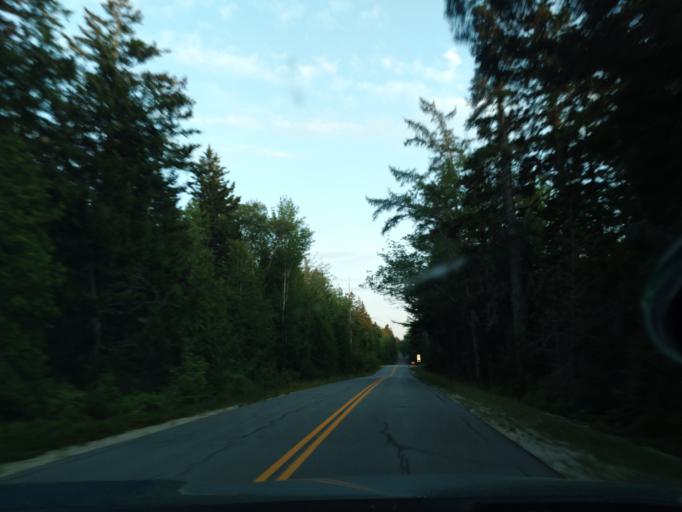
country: US
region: Maine
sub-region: Hancock County
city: Gouldsboro
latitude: 44.3854
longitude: -68.0697
